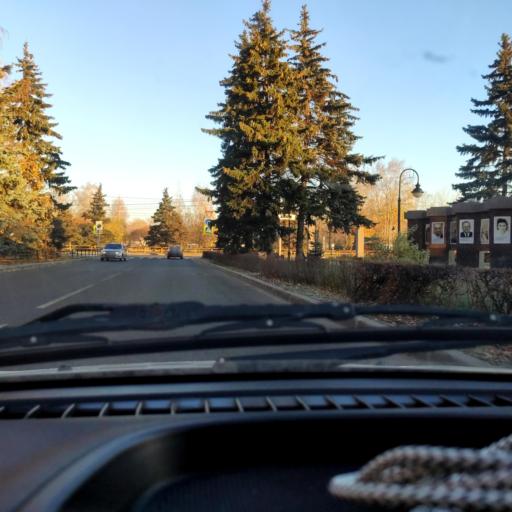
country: RU
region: Samara
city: Tol'yatti
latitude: 53.5079
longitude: 49.4185
